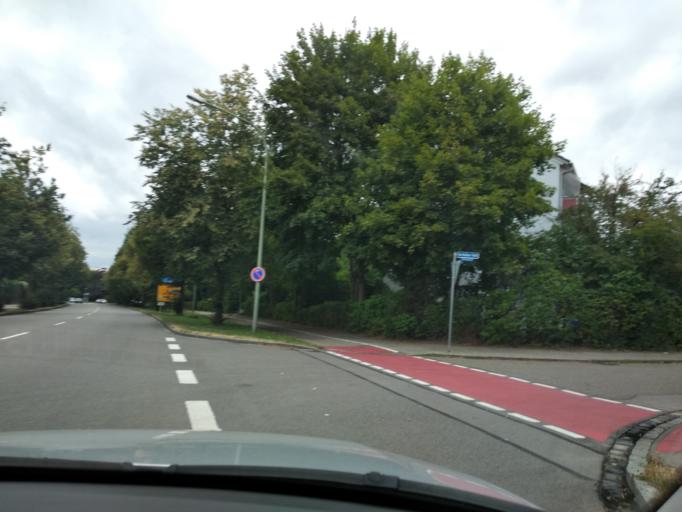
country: DE
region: Bavaria
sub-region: Swabia
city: Memmingen
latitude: 47.9932
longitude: 10.1994
